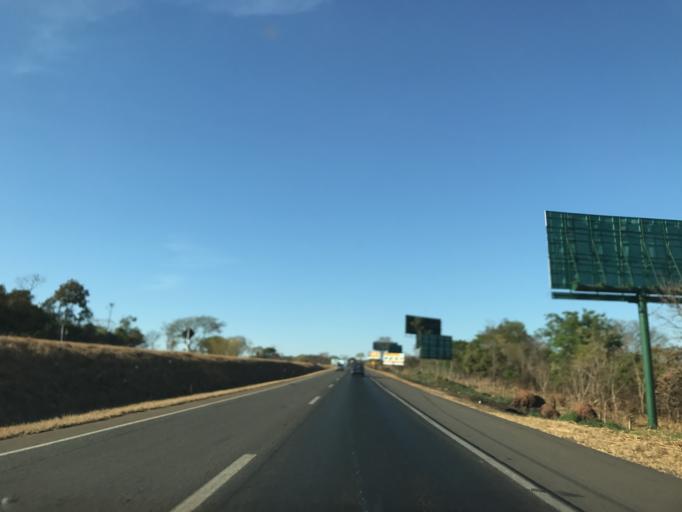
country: BR
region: Goias
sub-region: Hidrolandia
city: Hidrolandia
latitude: -16.9122
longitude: -49.2534
